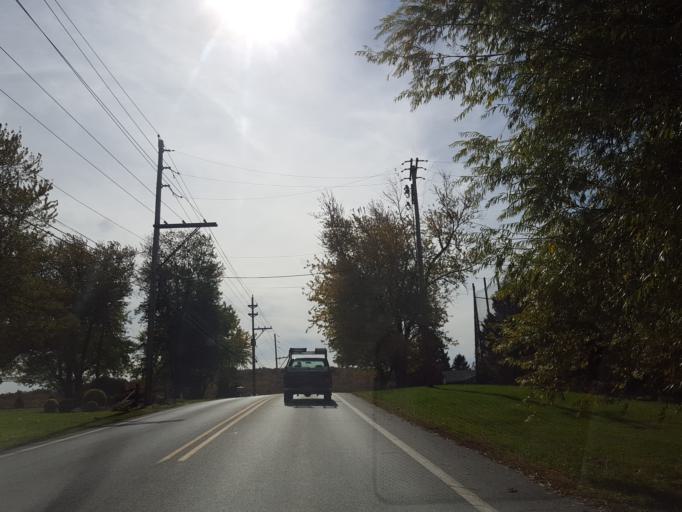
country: US
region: Pennsylvania
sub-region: York County
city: Windsor
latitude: 39.9530
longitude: -76.5906
